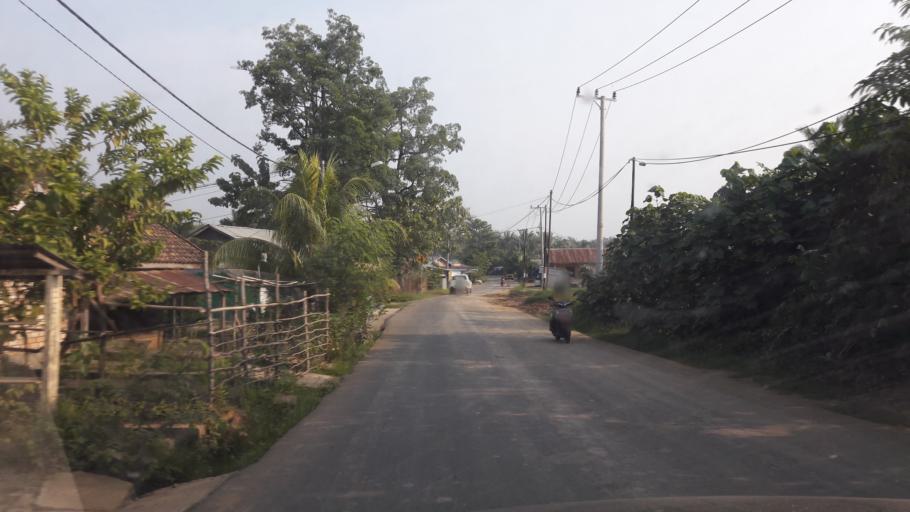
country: ID
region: South Sumatra
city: Gunungmegang Dalam
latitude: -3.2704
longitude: 103.8277
